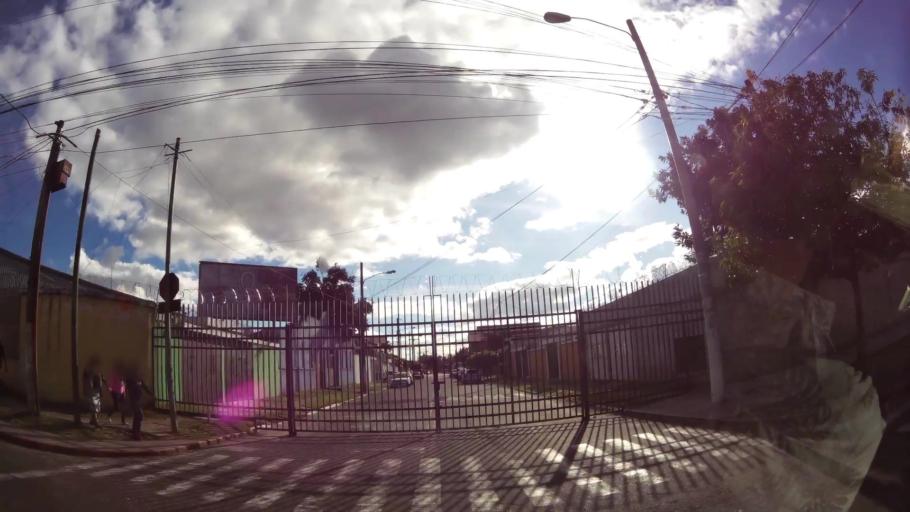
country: GT
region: Guatemala
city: Guatemala City
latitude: 14.6189
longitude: -90.5529
